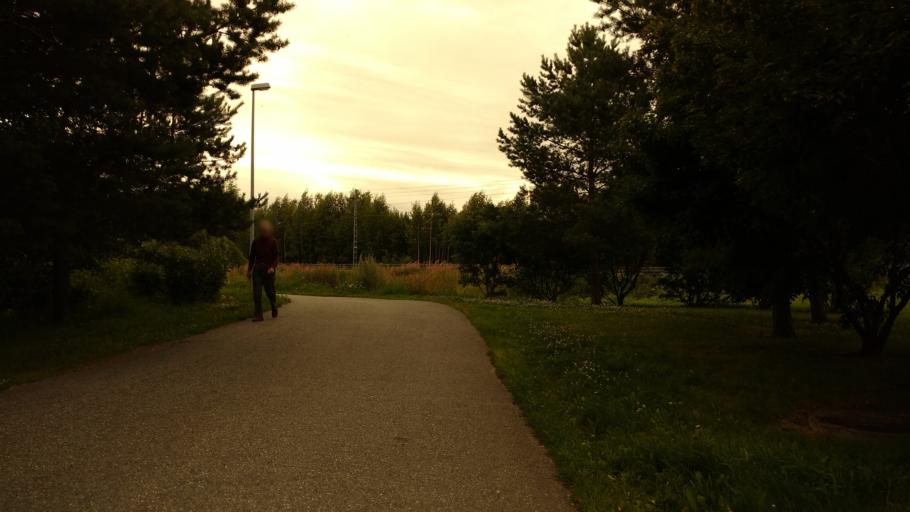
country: FI
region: Varsinais-Suomi
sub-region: Turku
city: Kaarina
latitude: 60.4380
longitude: 22.3382
